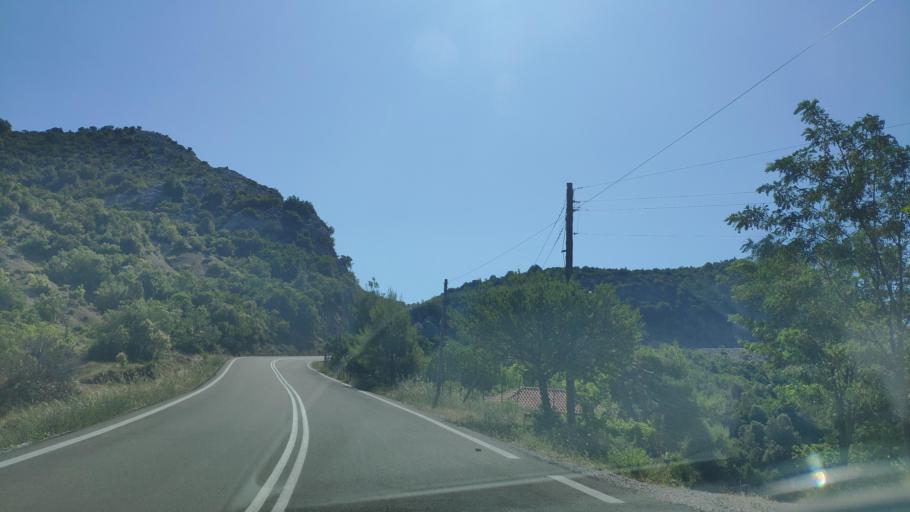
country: GR
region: West Greece
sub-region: Nomos Aitolias kai Akarnanias
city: Sardinia
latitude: 38.9249
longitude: 21.4169
